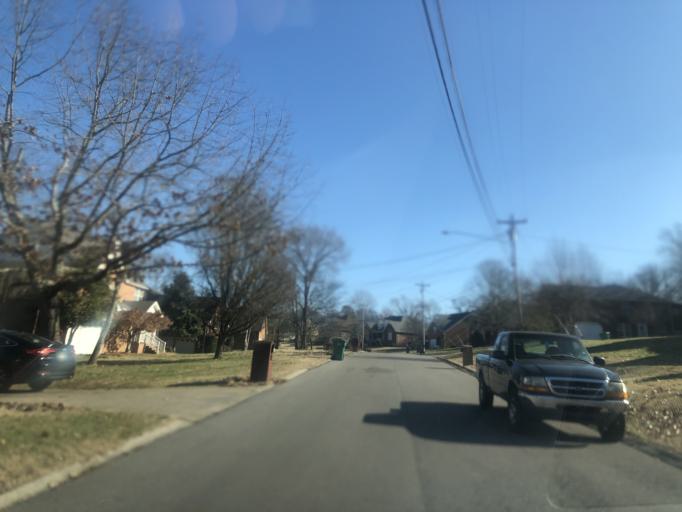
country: US
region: Tennessee
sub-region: Rutherford County
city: Smyrna
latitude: 35.9719
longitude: -86.5388
